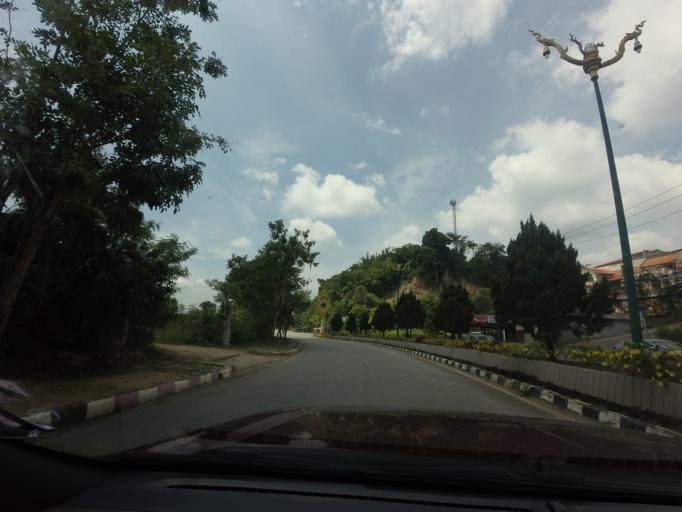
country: TH
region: Yala
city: Betong
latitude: 5.7737
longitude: 101.0629
